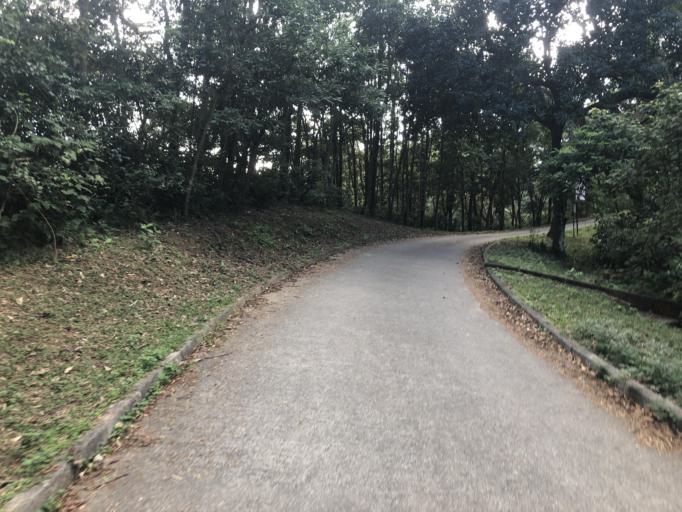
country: HK
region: Tsuen Wan
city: Tsuen Wan
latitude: 22.4039
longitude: 114.0976
